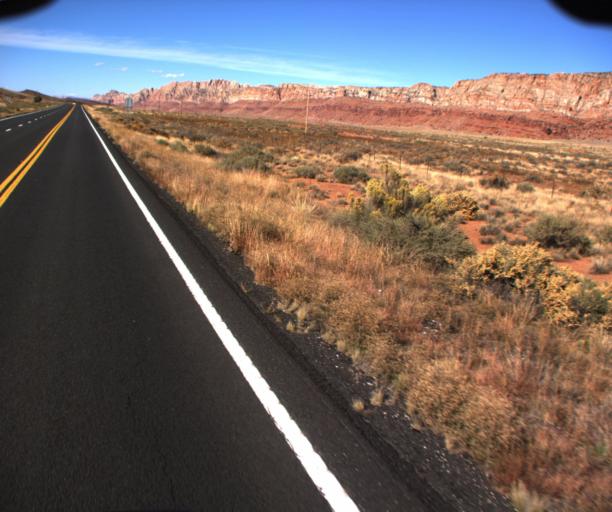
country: US
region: Arizona
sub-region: Coconino County
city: LeChee
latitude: 36.4500
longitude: -111.5596
